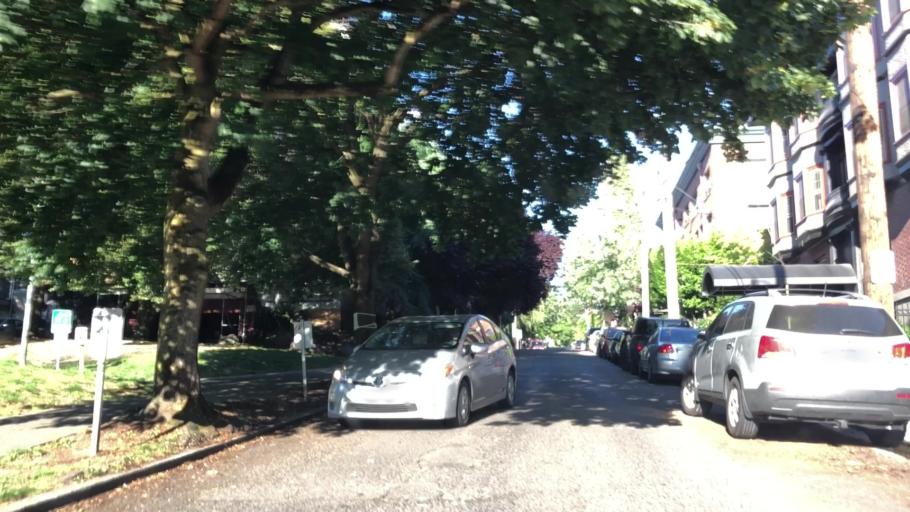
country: US
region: Washington
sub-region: King County
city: Seattle
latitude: 47.6209
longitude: -122.3266
